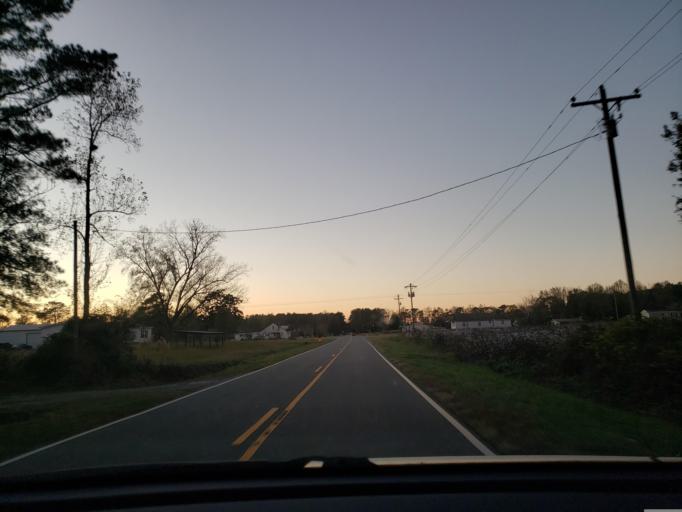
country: US
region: North Carolina
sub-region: Duplin County
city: Beulaville
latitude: 34.7938
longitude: -77.7675
